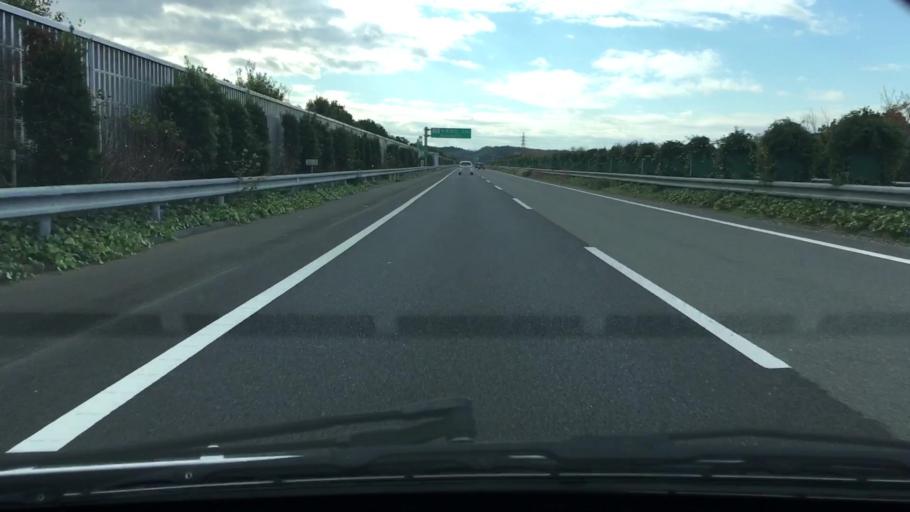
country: JP
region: Chiba
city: Kisarazu
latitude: 35.4039
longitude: 140.0077
